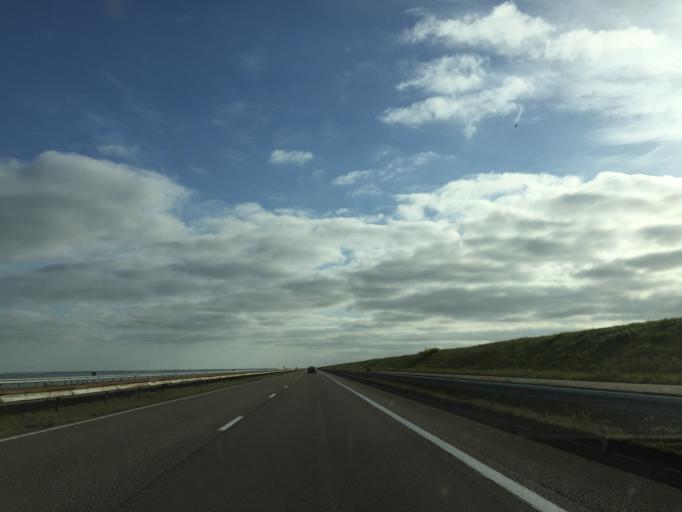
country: NL
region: North Holland
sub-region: Gemeente Hollands Kroon
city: Den Oever
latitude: 53.0042
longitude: 5.1753
